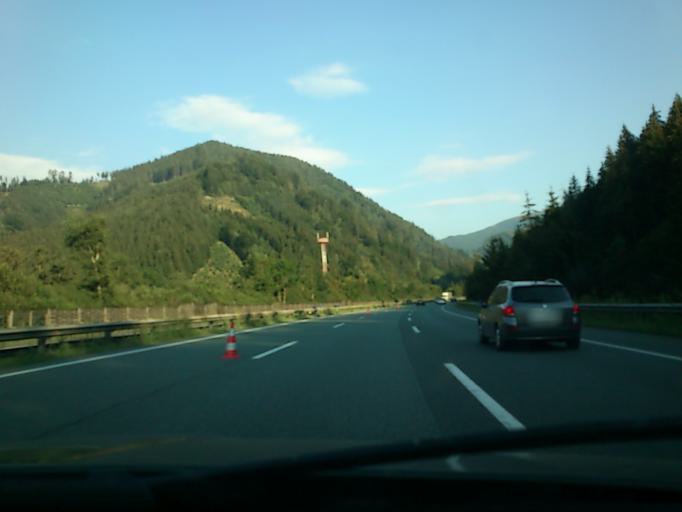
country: AT
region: Styria
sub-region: Politischer Bezirk Leoben
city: Sankt Michael in Obersteiermark
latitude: 47.3162
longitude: 15.0509
